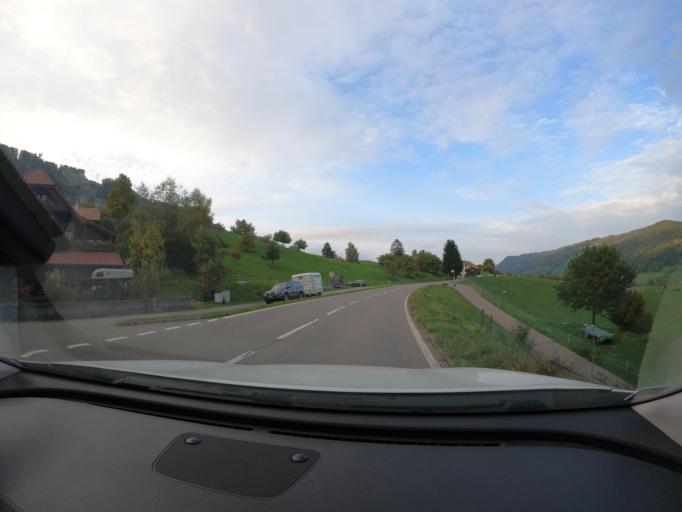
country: CH
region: Bern
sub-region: Bern-Mittelland District
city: Hermiswil
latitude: 46.8394
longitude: 7.4924
